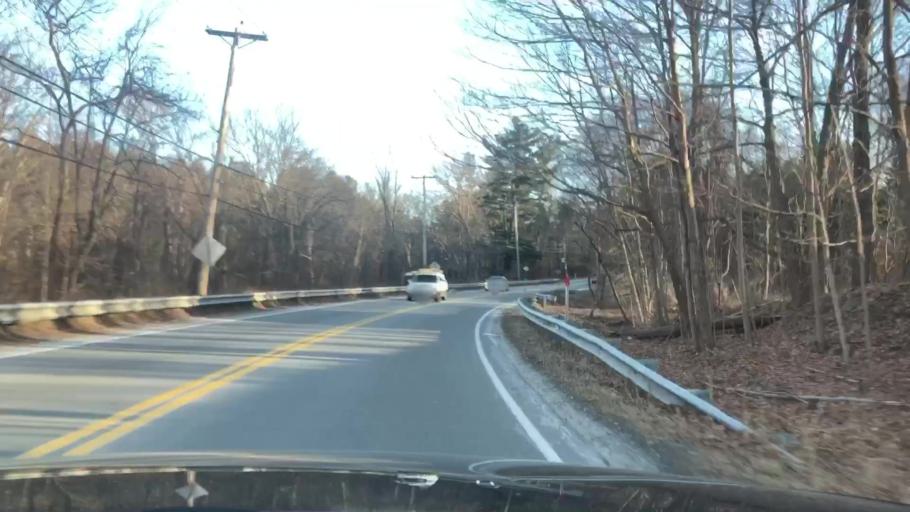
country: US
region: Massachusetts
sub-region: Worcester County
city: Bolton
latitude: 42.4454
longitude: -71.6250
